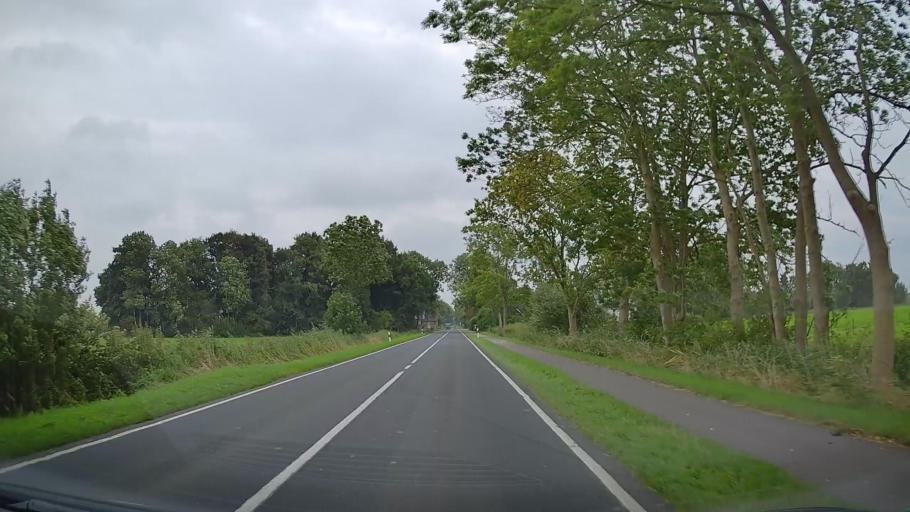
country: DE
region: Lower Saxony
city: Freiburg
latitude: 53.8131
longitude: 9.3024
